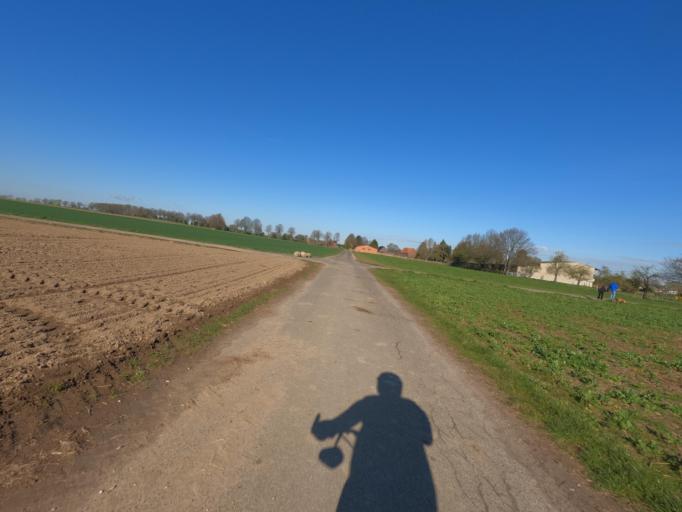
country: DE
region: North Rhine-Westphalia
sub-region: Regierungsbezirk Koln
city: Gangelt
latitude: 50.9977
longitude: 6.0507
